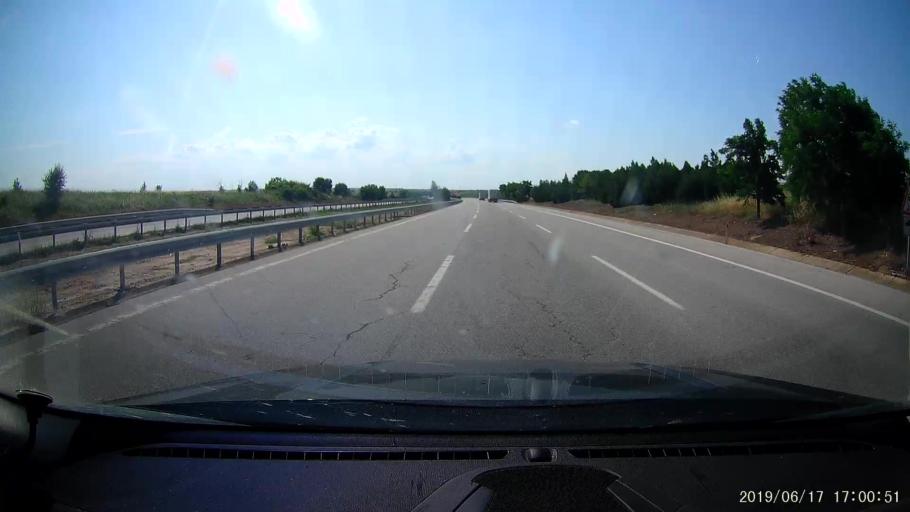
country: TR
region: Edirne
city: Haskoy
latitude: 41.6248
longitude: 26.8198
